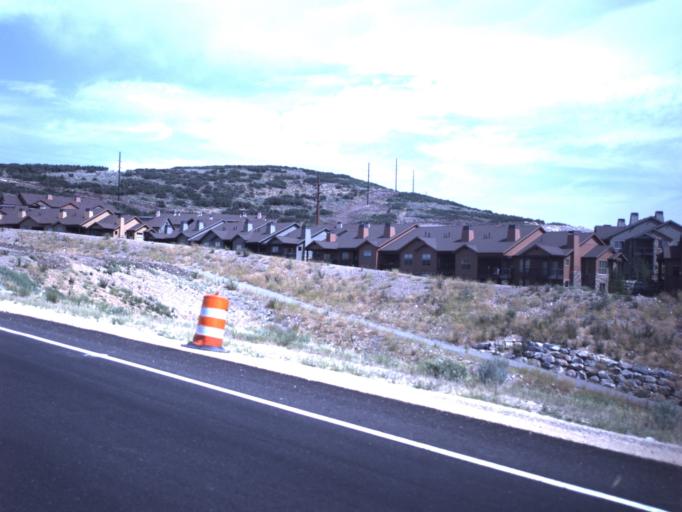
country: US
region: Utah
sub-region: Summit County
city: Park City
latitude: 40.6793
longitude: -111.4337
